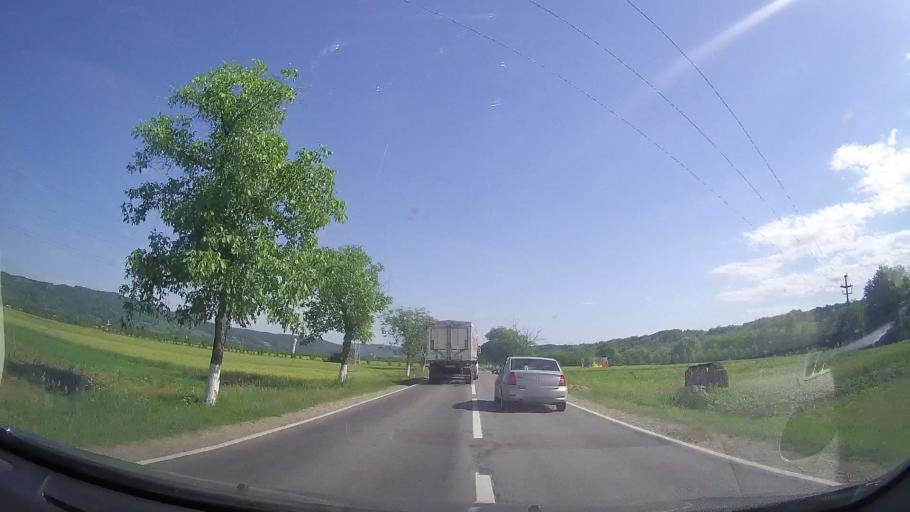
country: RO
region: Prahova
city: Drajna de Jos
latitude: 45.2335
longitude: 26.0296
